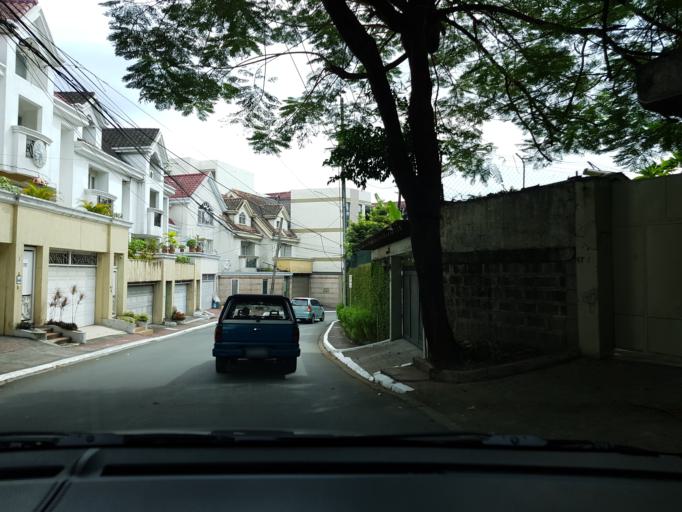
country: PH
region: Metro Manila
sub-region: San Juan
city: San Juan
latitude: 14.6115
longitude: 121.0410
